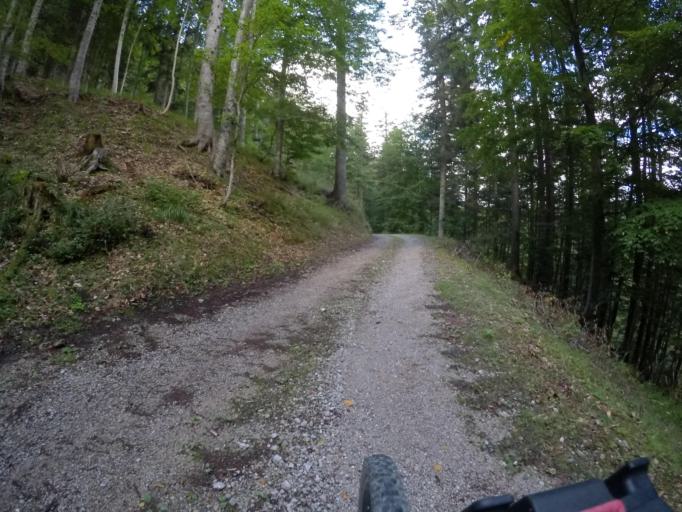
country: IT
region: Friuli Venezia Giulia
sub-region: Provincia di Udine
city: Paularo
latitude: 46.4979
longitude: 13.1775
